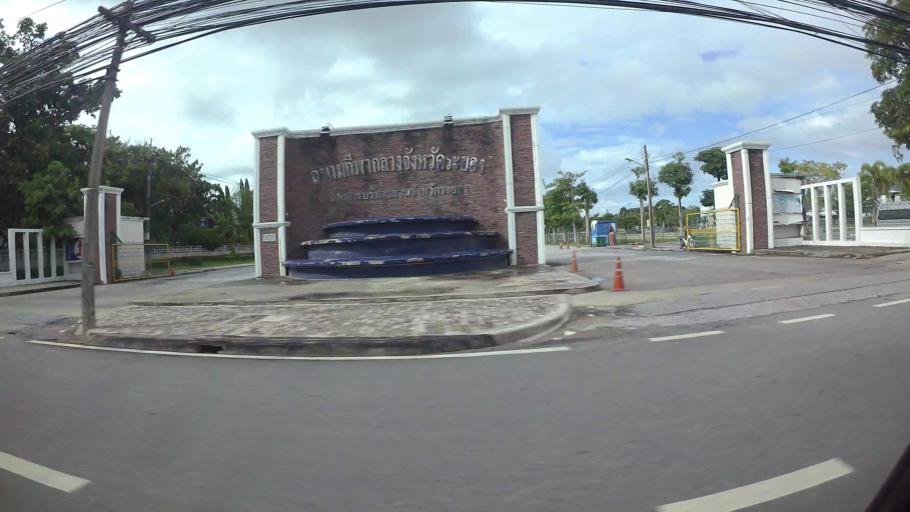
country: TH
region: Rayong
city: Rayong
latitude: 12.6832
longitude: 101.2352
